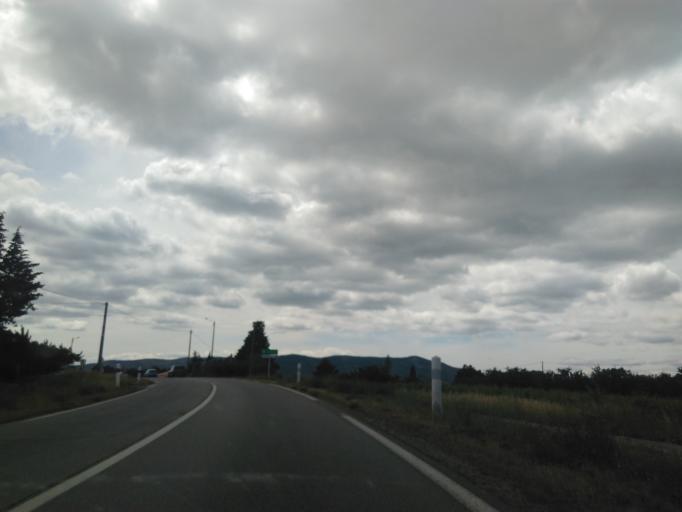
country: FR
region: Rhone-Alpes
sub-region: Departement de l'Ardeche
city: Alba-la-Romaine
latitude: 44.5745
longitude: 4.6271
